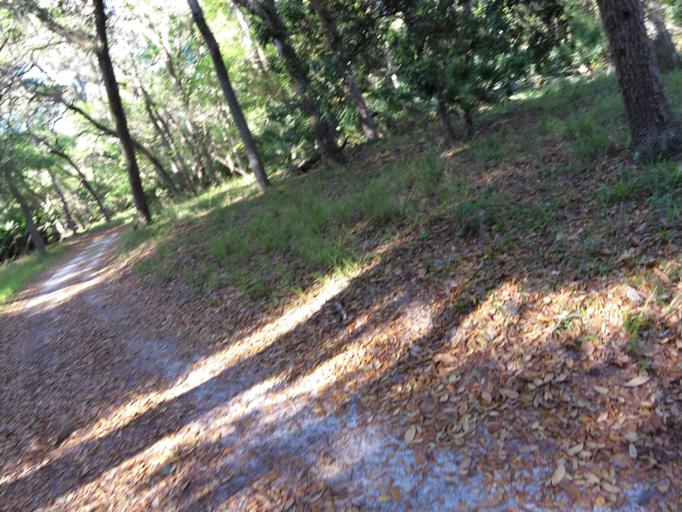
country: US
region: Florida
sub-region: Saint Johns County
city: Villano Beach
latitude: 30.0185
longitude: -81.3337
